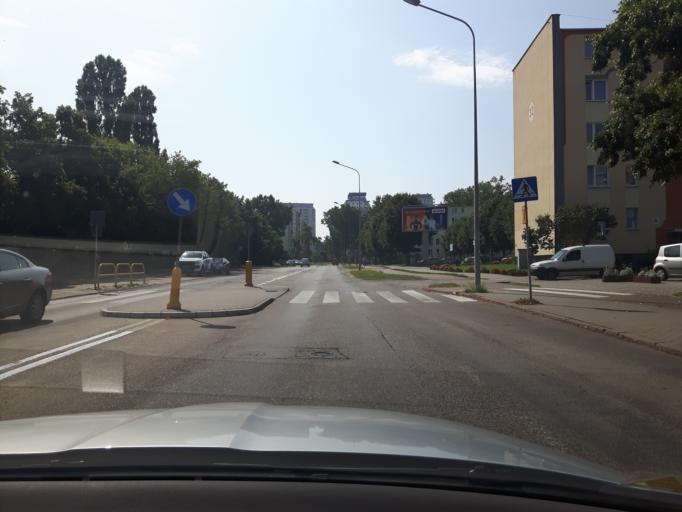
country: PL
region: Pomeranian Voivodeship
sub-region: Sopot
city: Sopot
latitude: 54.4091
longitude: 18.6049
